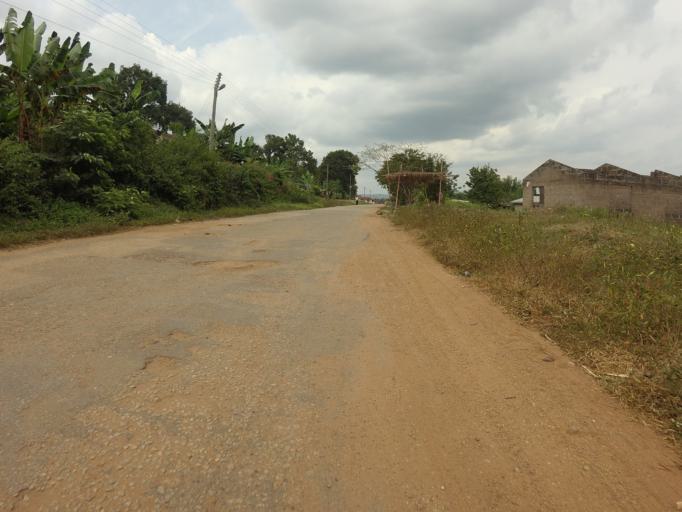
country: GH
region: Volta
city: Ho
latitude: 6.6475
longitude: 0.3384
